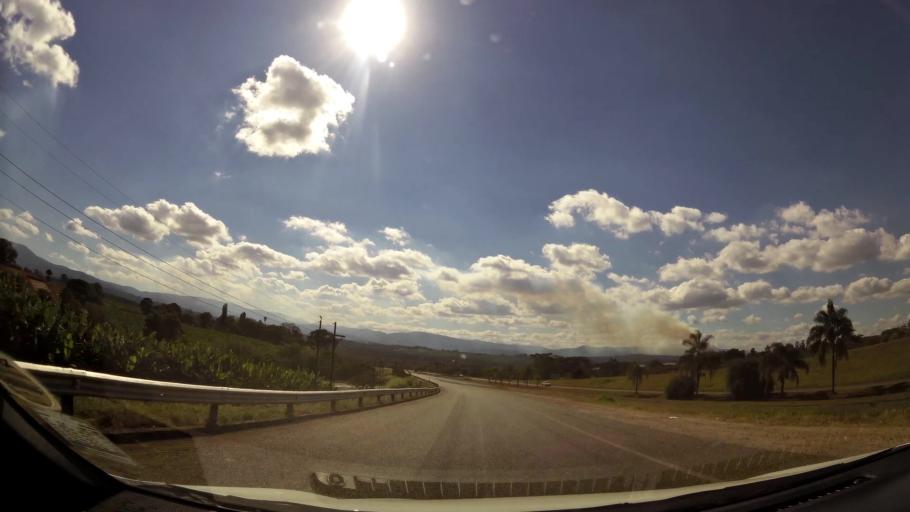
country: ZA
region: Limpopo
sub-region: Mopani District Municipality
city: Tzaneen
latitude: -23.8349
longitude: 30.1355
